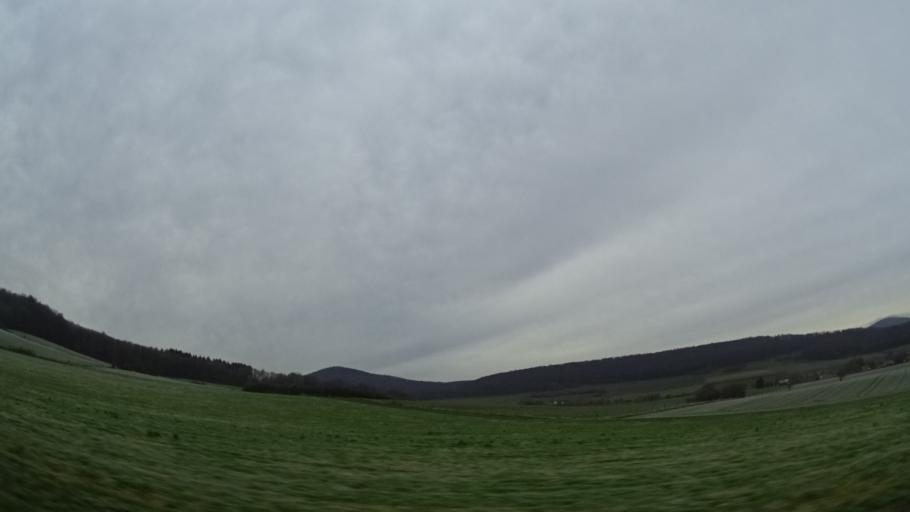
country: DE
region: Hesse
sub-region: Regierungsbezirk Kassel
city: Rasdorf
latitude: 50.7320
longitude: 9.9198
